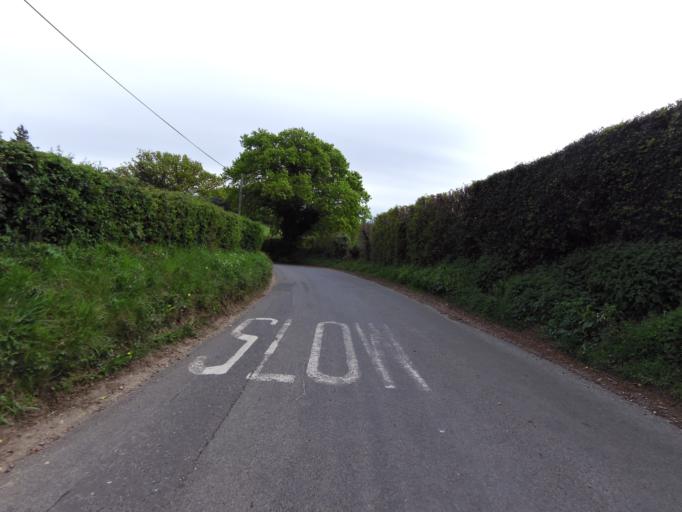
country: GB
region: England
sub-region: Suffolk
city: Ipswich
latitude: 51.9739
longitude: 1.1682
